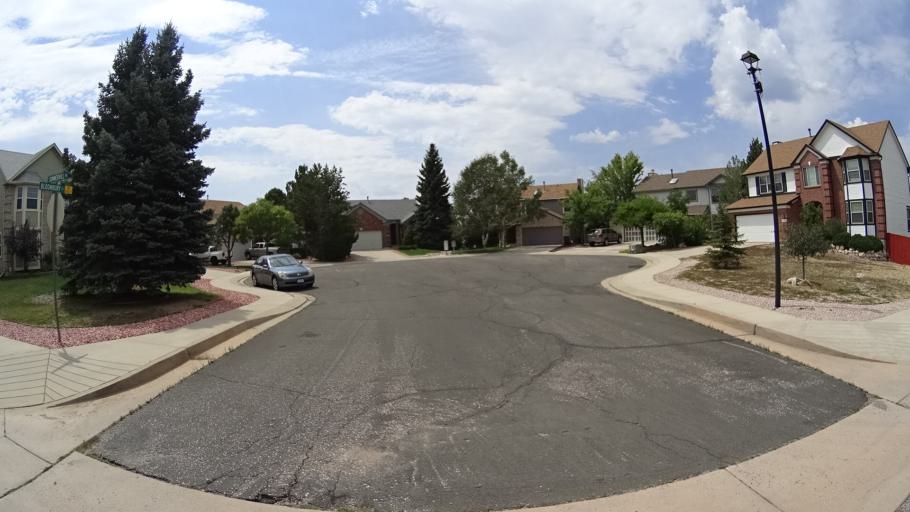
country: US
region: Colorado
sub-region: El Paso County
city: Black Forest
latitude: 38.9608
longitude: -104.7752
